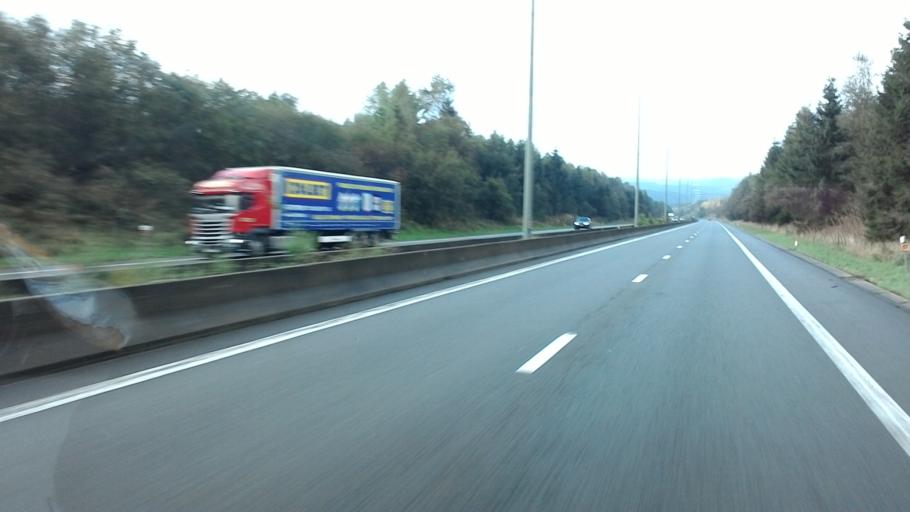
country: BE
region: Wallonia
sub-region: Province du Luxembourg
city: Manhay
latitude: 50.2723
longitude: 5.7271
